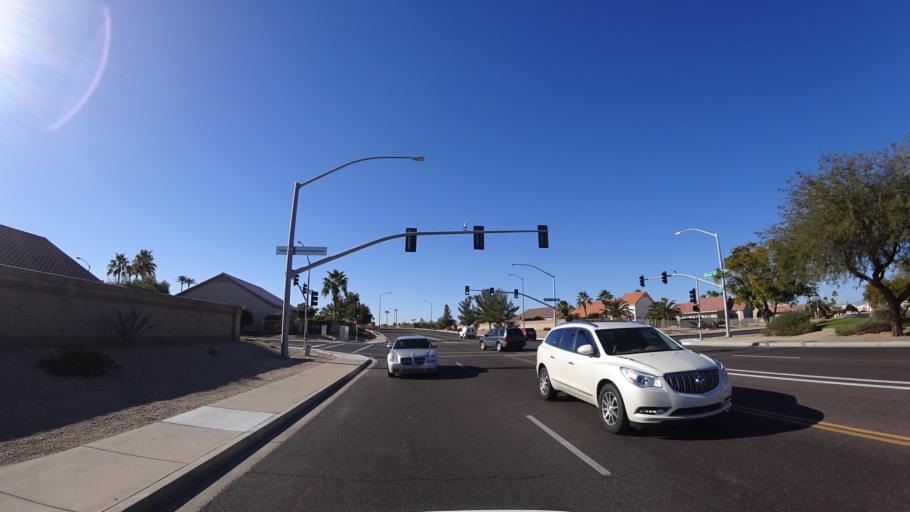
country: US
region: Arizona
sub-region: Maricopa County
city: Sun City West
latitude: 33.6869
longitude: -112.3590
